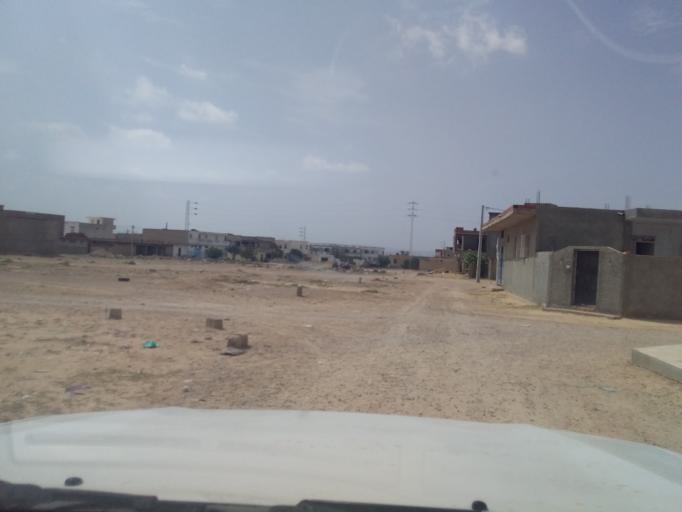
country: TN
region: Qabis
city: Matmata
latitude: 33.6206
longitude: 10.2730
